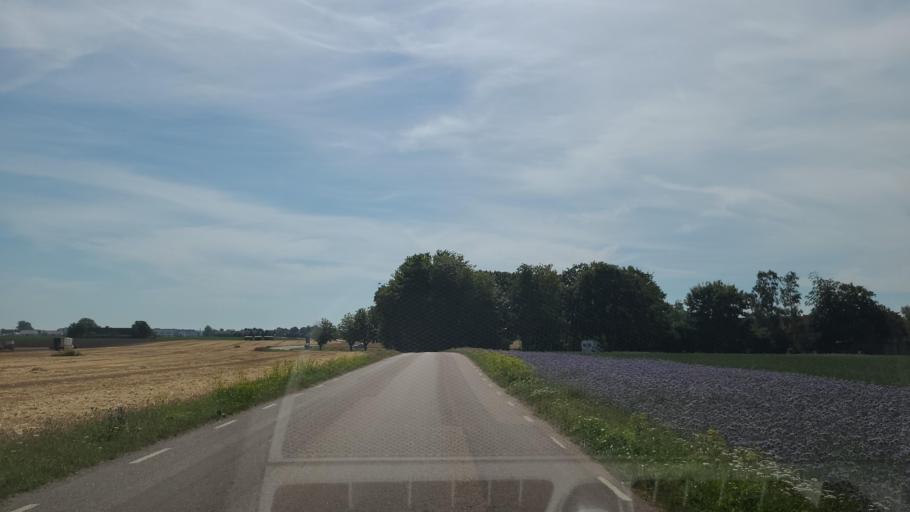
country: SE
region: Skane
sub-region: Trelleborgs Kommun
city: Skare
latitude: 55.4152
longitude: 13.0833
